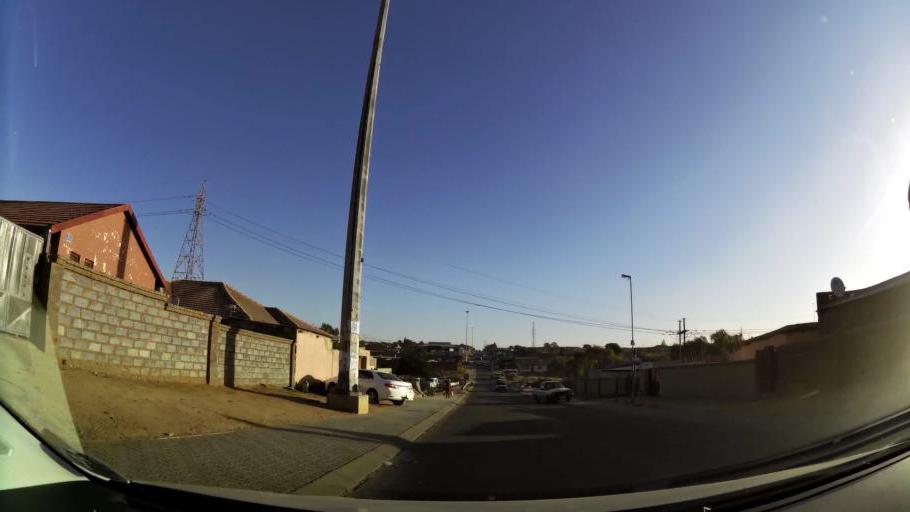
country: ZA
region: Gauteng
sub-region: Ekurhuleni Metropolitan Municipality
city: Tembisa
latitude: -26.0217
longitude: 28.2050
